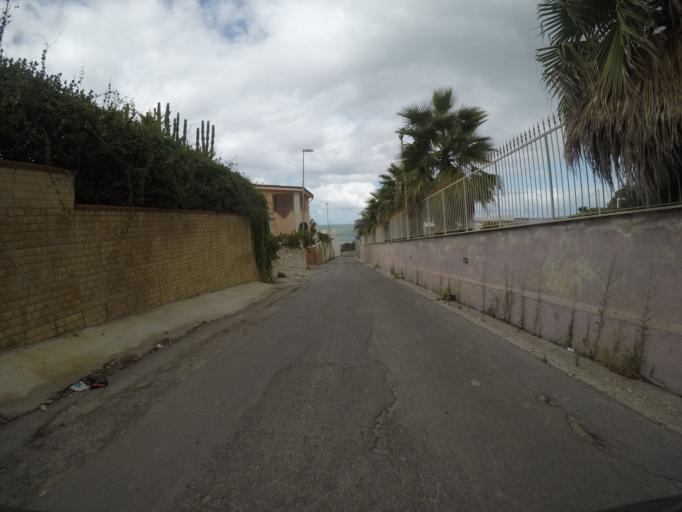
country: IT
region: Sicily
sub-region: Palermo
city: Trappeto
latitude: 38.0720
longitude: 13.0547
